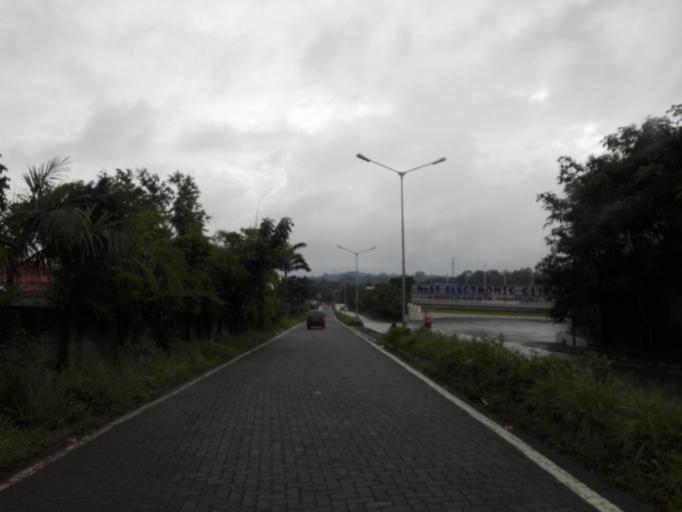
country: IN
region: Kerala
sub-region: Ernakulam
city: Aluva
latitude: 10.0565
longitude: 76.3593
